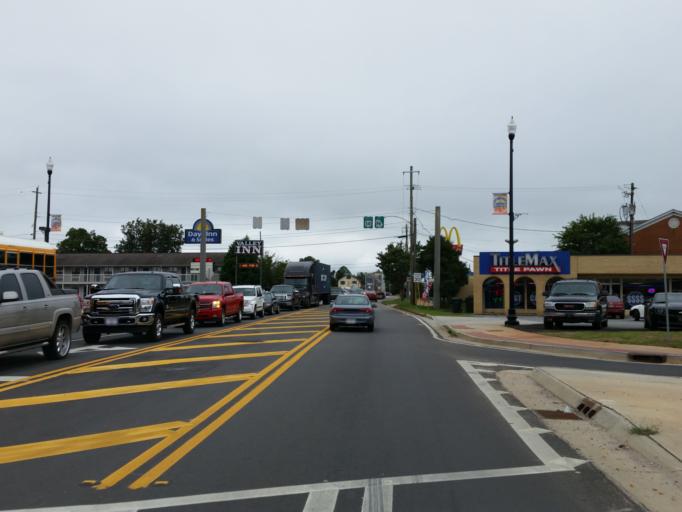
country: US
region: Georgia
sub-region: Peach County
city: Fort Valley
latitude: 32.5583
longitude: -83.8836
